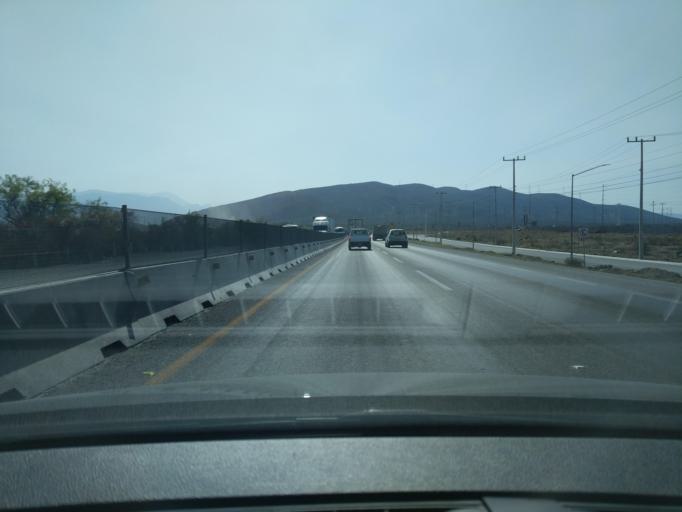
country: MX
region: Nuevo Leon
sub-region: Garcia
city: Los Parques
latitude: 25.7668
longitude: -100.4872
